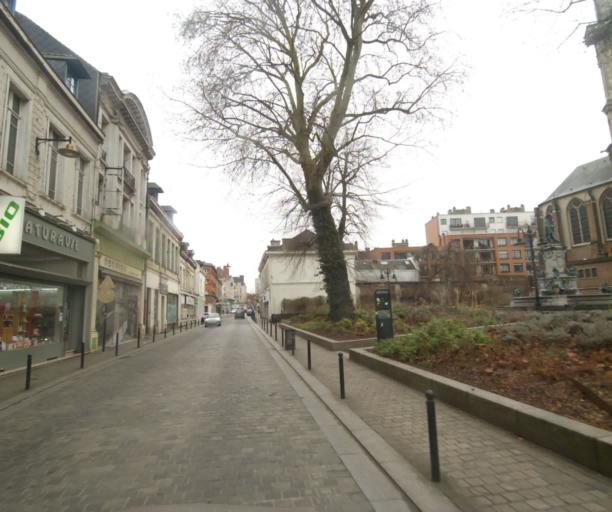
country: FR
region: Nord-Pas-de-Calais
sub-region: Departement du Nord
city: Valenciennes
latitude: 50.3593
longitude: 3.5204
